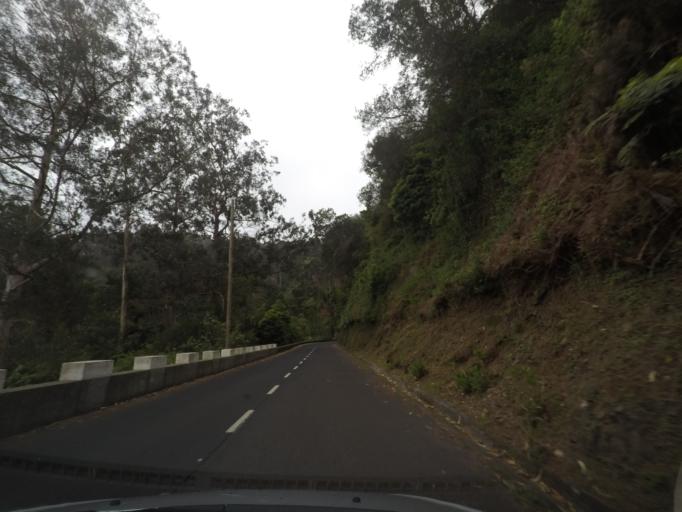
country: PT
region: Madeira
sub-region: Santana
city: Santana
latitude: 32.7498
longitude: -16.8331
